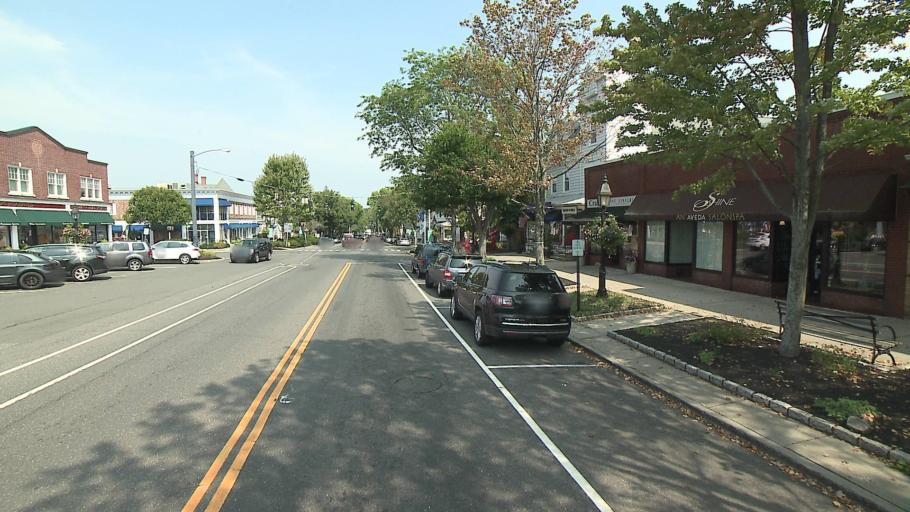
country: US
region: Connecticut
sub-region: Fairfield County
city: Ridgefield
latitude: 41.2810
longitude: -73.4984
